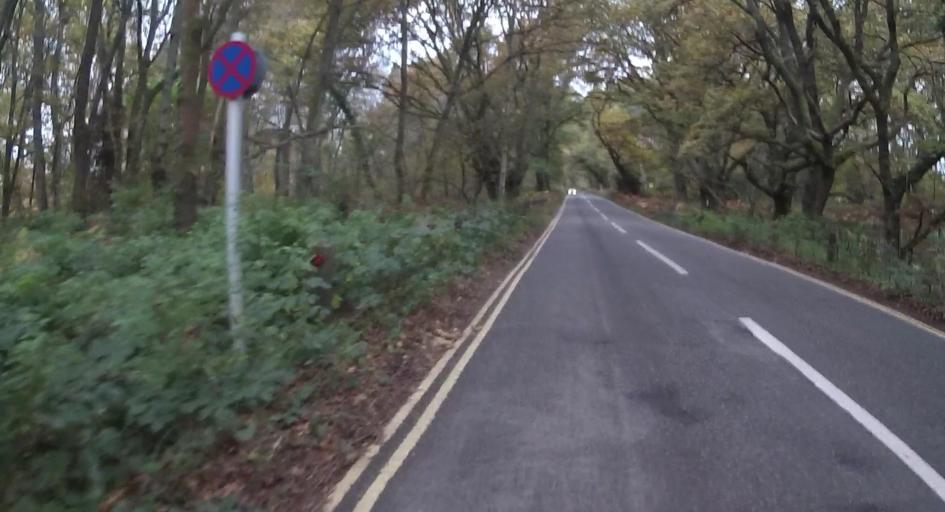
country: GB
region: England
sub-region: Surrey
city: Churt
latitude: 51.1590
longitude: -0.7953
